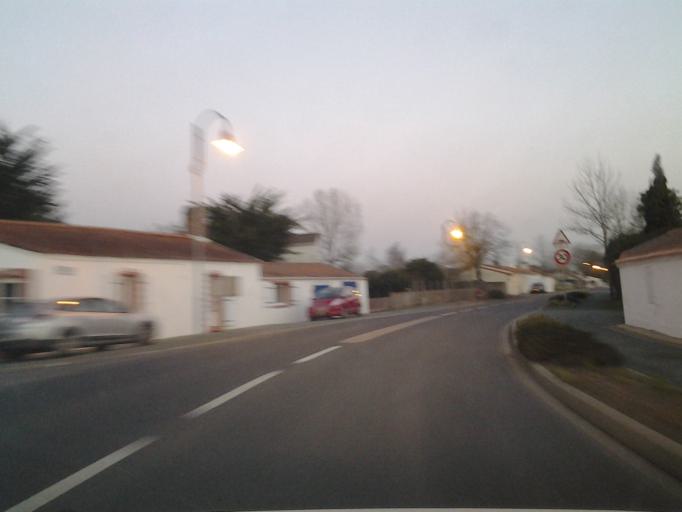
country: FR
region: Pays de la Loire
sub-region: Departement de la Vendee
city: Saint-Gervais
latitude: 46.9011
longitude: -1.9898
